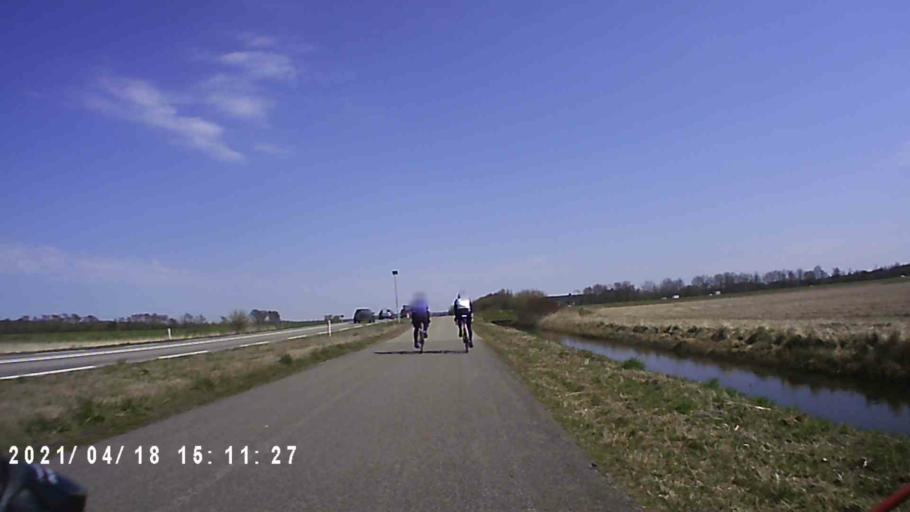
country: NL
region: Groningen
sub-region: Gemeente De Marne
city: Ulrum
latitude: 53.3646
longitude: 6.2564
